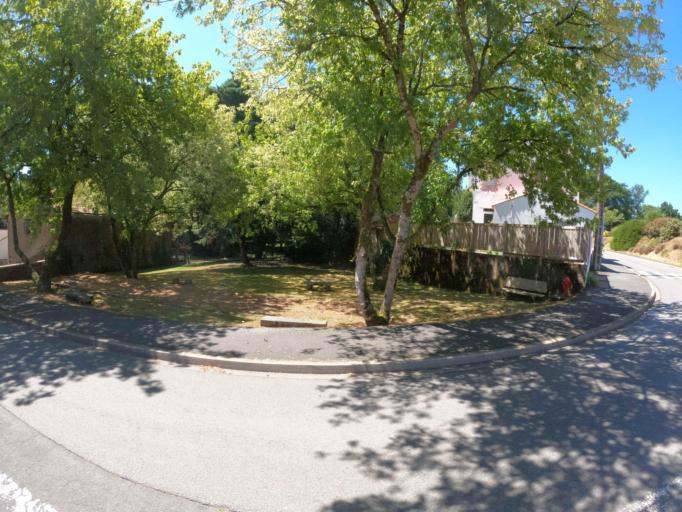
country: FR
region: Pays de la Loire
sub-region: Departement de la Loire-Atlantique
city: La Limouziniere
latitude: 46.9635
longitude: -1.5831
